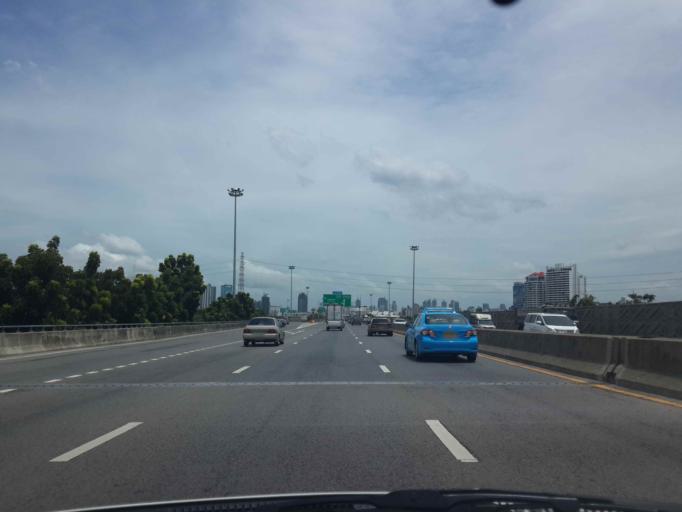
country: TH
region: Bangkok
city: Huai Khwang
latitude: 13.7628
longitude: 100.5989
